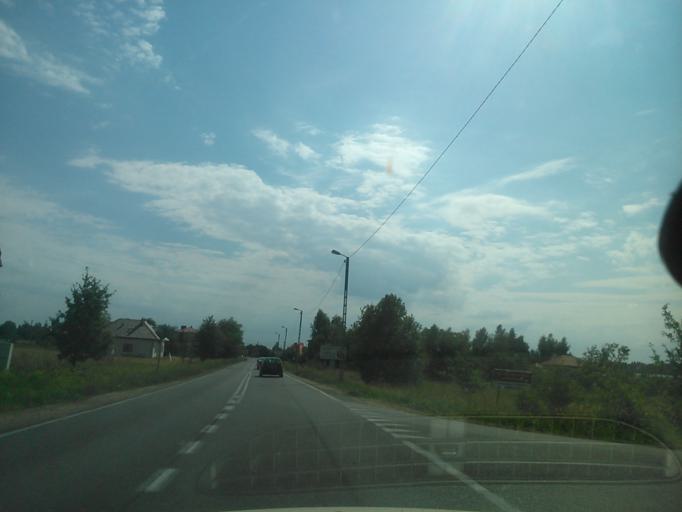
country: PL
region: Masovian Voivodeship
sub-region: Powiat mlawski
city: Mlawa
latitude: 53.1347
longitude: 20.3424
